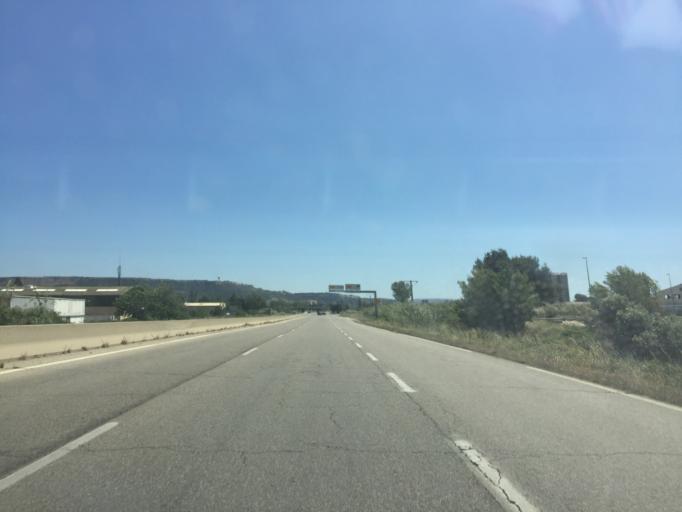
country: FR
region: Provence-Alpes-Cote d'Azur
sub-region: Departement des Bouches-du-Rhone
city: Rognac
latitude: 43.4983
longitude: 5.2140
